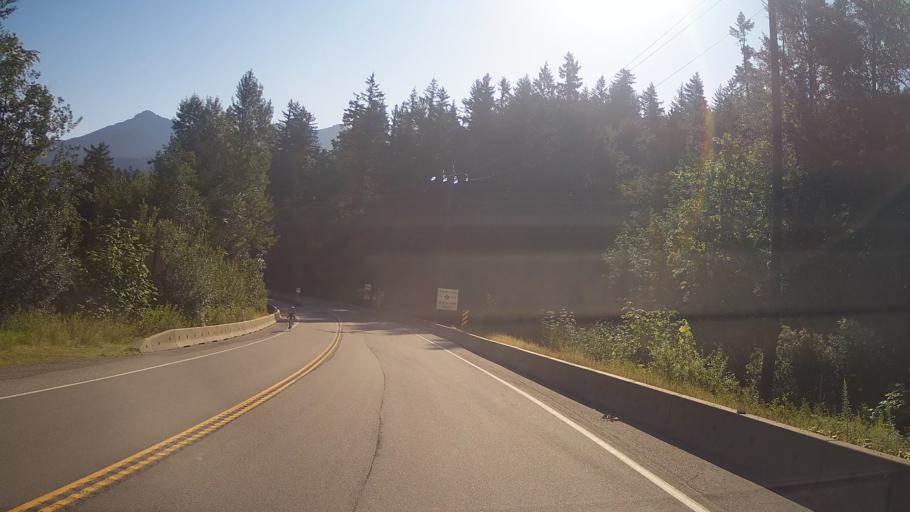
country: CA
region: British Columbia
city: Hope
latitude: 49.4085
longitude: -121.4483
